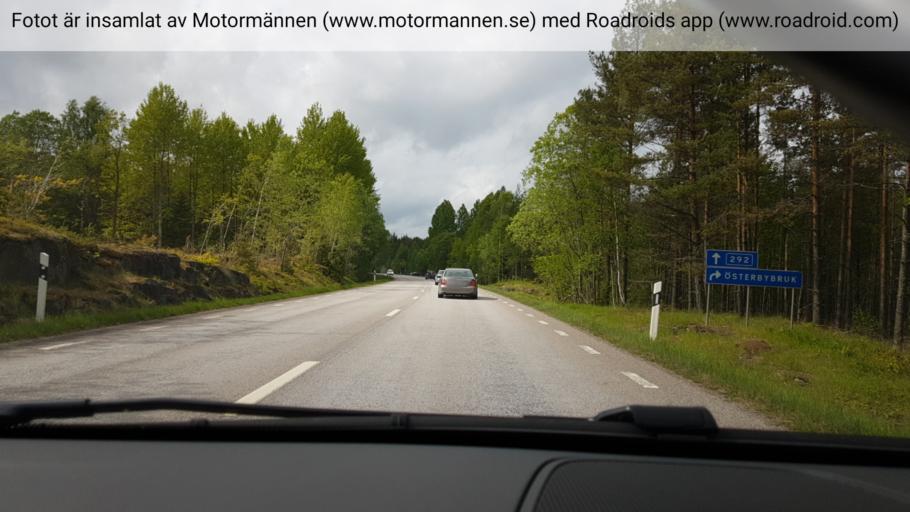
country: SE
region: Uppsala
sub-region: Osthammars Kommun
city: Osterbybruk
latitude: 60.1801
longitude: 17.9133
